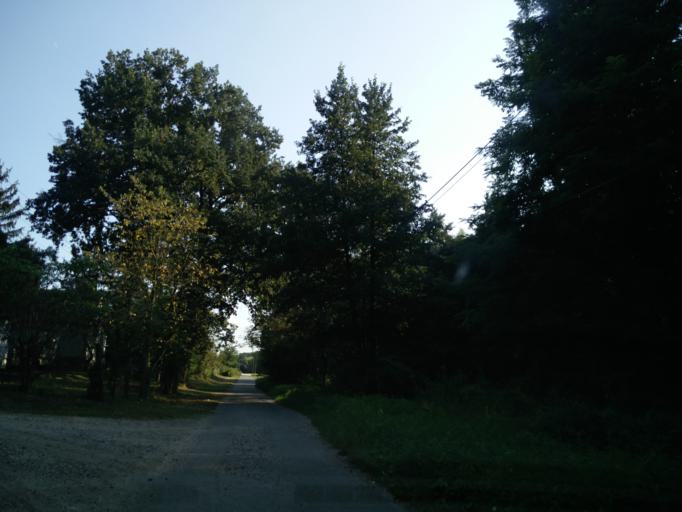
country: HU
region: Zala
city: Zalaegerszeg
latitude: 46.8724
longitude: 16.8489
